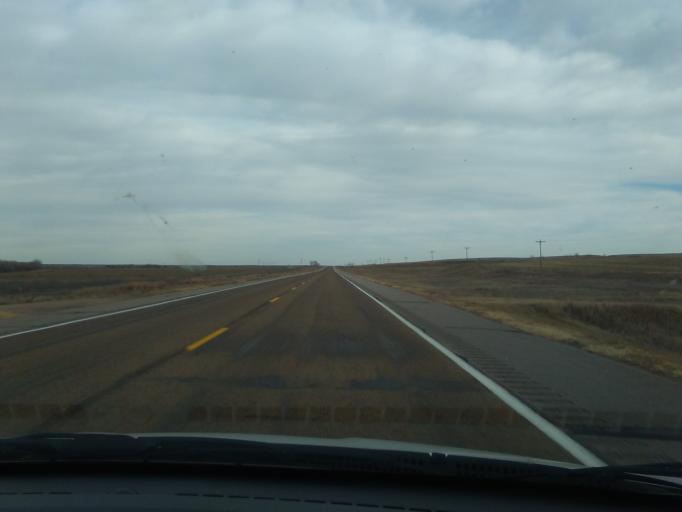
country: US
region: Kansas
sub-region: Cheyenne County
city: Saint Francis
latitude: 40.0181
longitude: -101.8970
